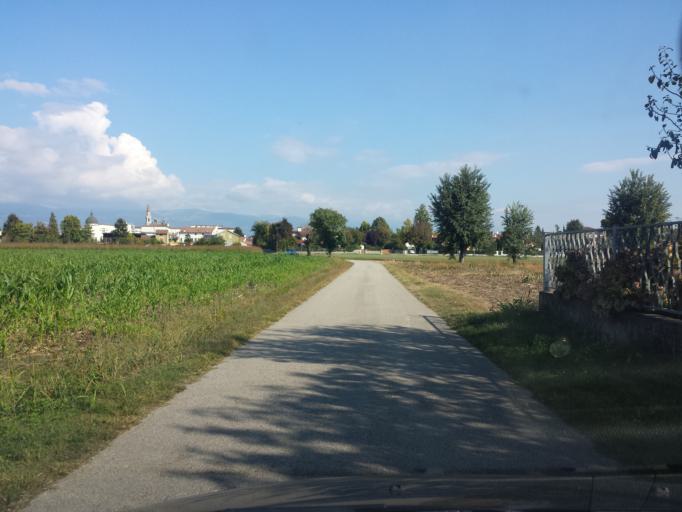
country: IT
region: Veneto
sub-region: Provincia di Vicenza
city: Sandrigo
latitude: 45.6524
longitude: 11.6013
